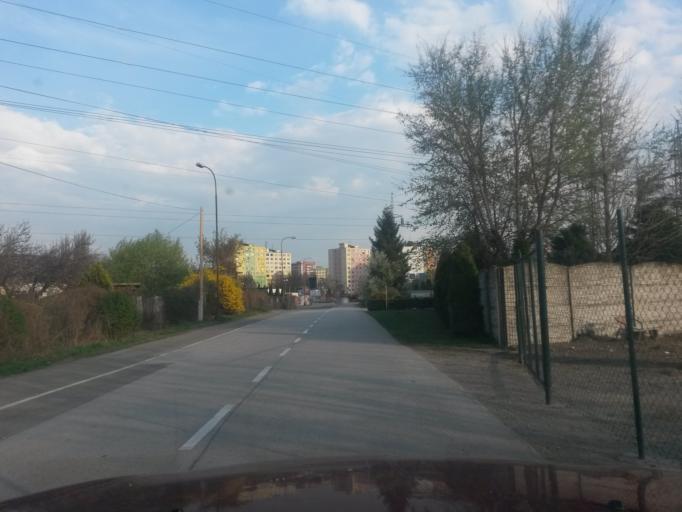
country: SK
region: Kosicky
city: Kosice
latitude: 48.6942
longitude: 21.2782
